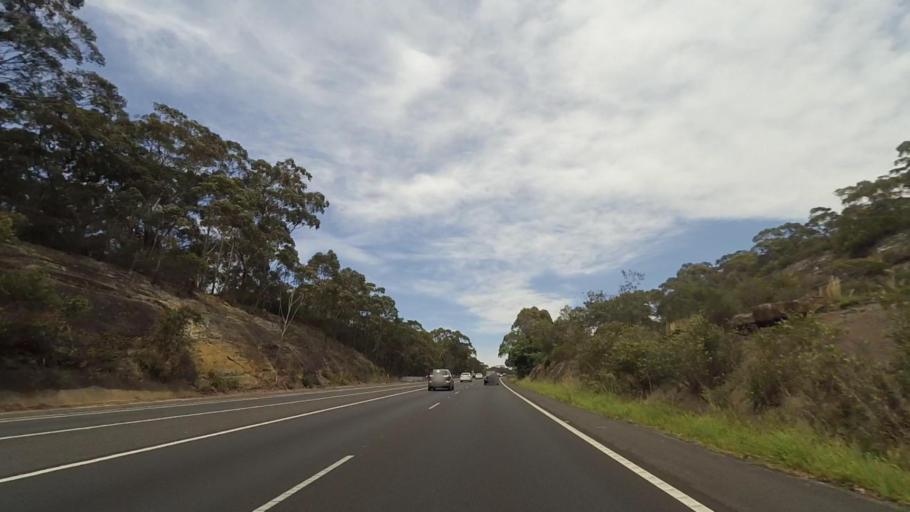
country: AU
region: New South Wales
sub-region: Wollongong
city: Helensburgh
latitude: -34.2044
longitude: 150.9648
